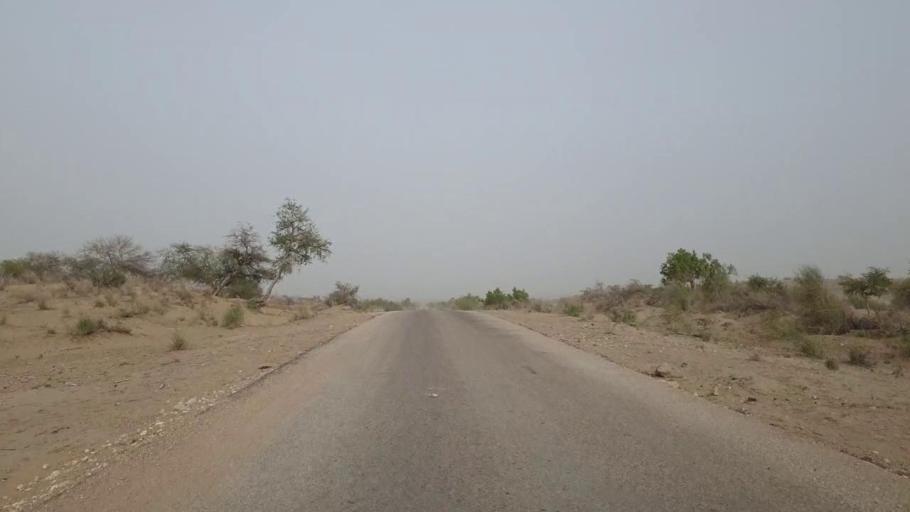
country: PK
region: Sindh
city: Islamkot
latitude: 24.5810
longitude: 70.3027
